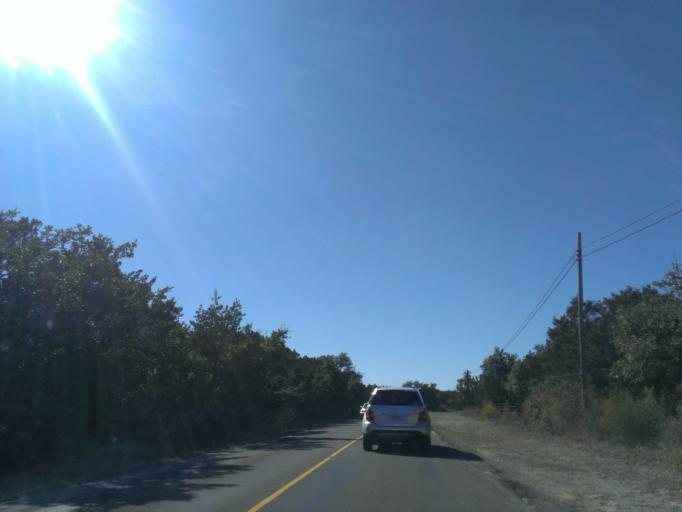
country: US
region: Texas
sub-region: Travis County
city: Briarcliff
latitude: 30.4613
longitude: -98.1305
